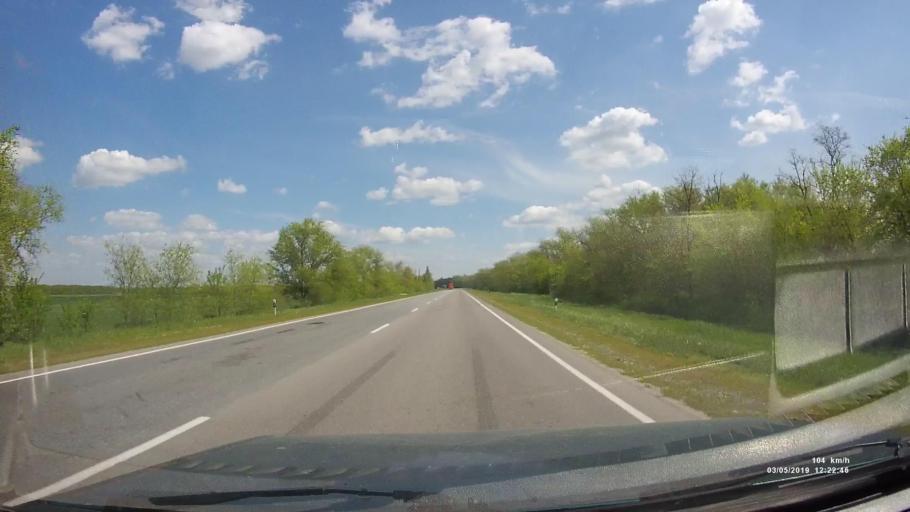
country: RU
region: Rostov
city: Semikarakorsk
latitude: 47.4065
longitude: 40.6686
